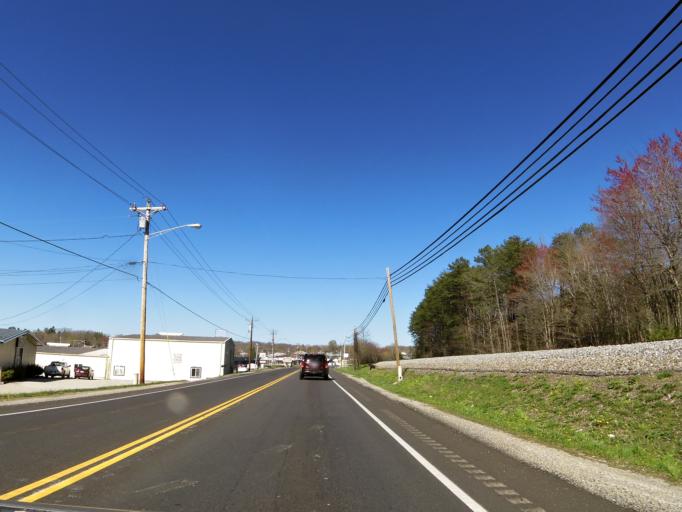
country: US
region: Tennessee
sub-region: Scott County
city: Oneida
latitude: 36.4951
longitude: -84.5217
